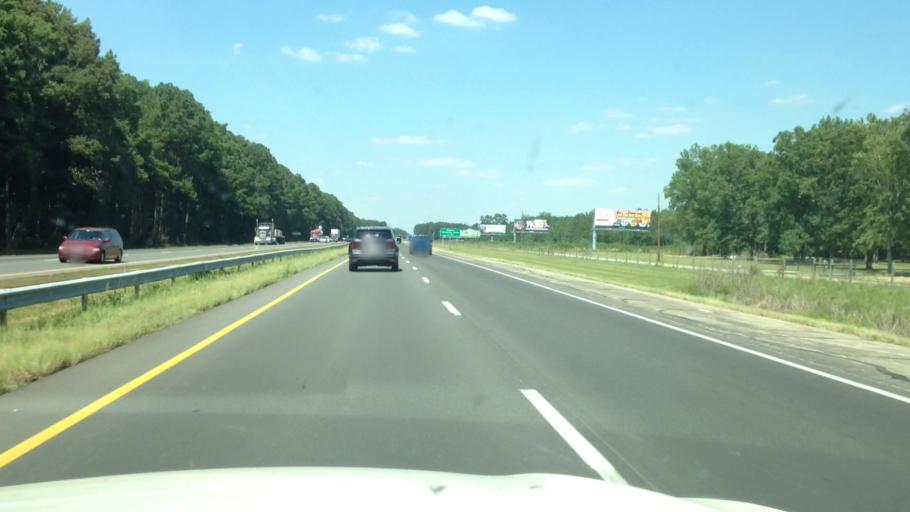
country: US
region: North Carolina
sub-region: Harnett County
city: Dunn
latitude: 35.1930
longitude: -78.6802
